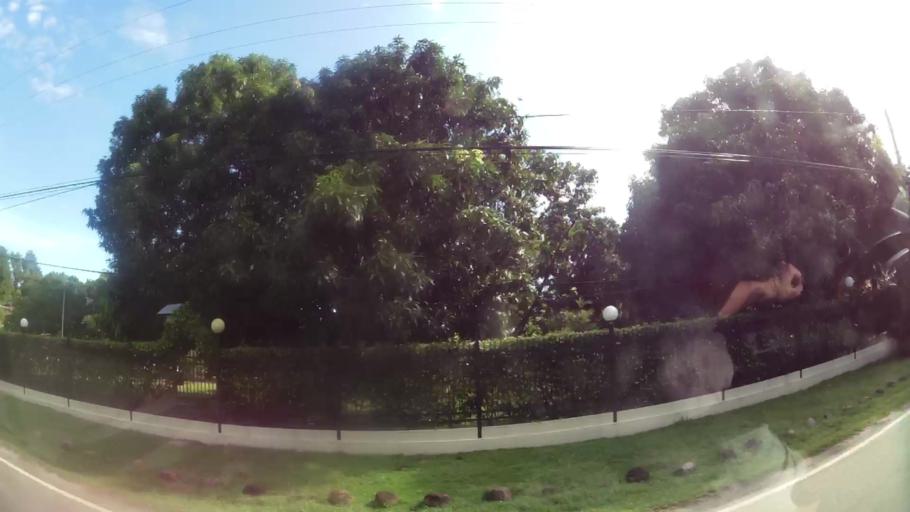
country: PA
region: Panama
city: Nueva Gorgona
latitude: 8.5289
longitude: -79.8932
